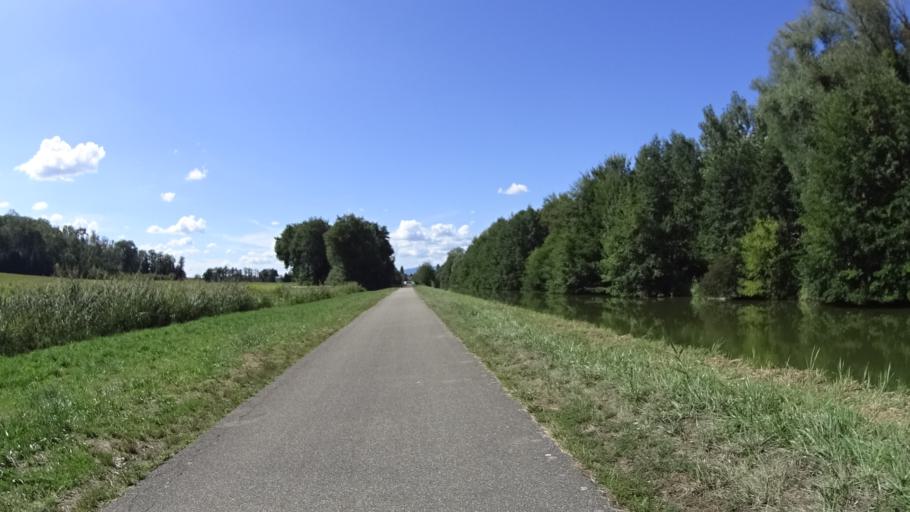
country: FR
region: Alsace
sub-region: Departement du Haut-Rhin
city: Aspach
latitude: 47.6585
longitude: 7.2154
